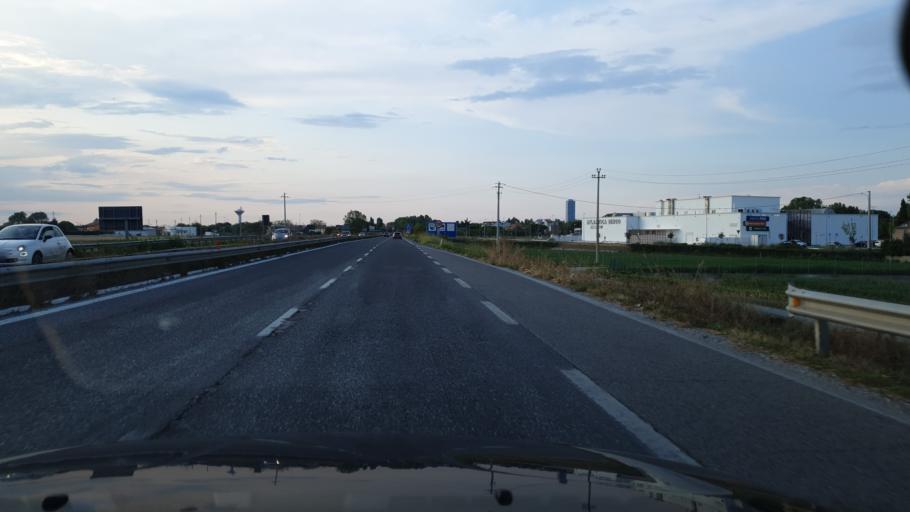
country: IT
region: Emilia-Romagna
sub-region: Forli-Cesena
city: Cesenatico
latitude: 44.1810
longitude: 12.4119
